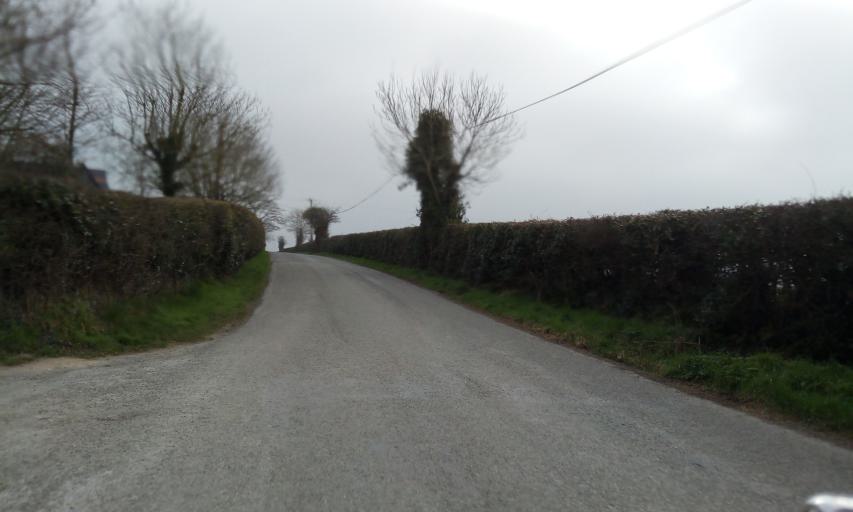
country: IE
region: Leinster
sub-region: Kilkenny
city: Kilkenny
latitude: 52.6584
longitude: -7.1721
